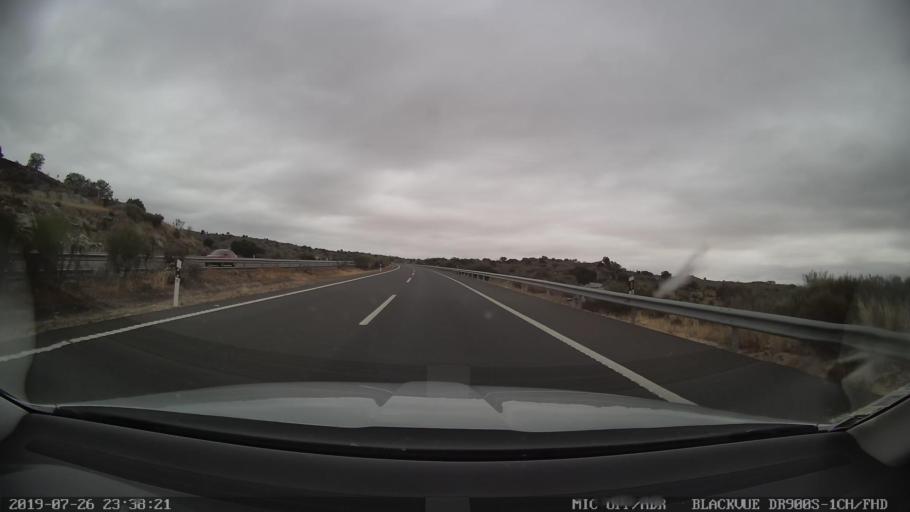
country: ES
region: Extremadura
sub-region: Provincia de Caceres
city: Trujillo
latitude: 39.4292
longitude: -5.8780
